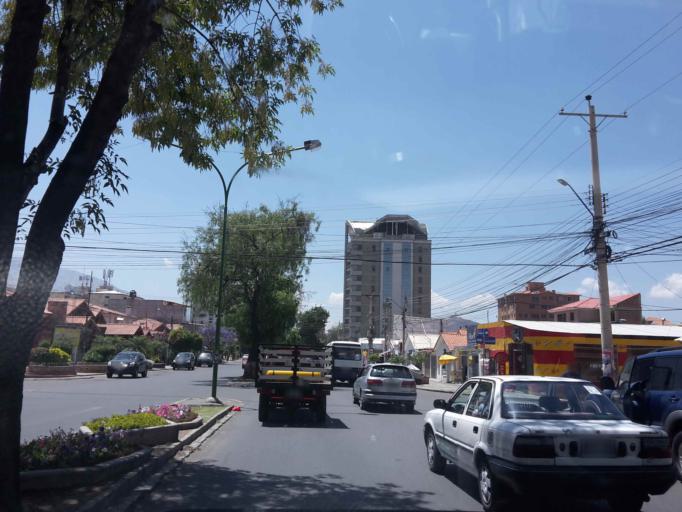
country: BO
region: Cochabamba
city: Cochabamba
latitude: -17.3718
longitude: -66.1753
